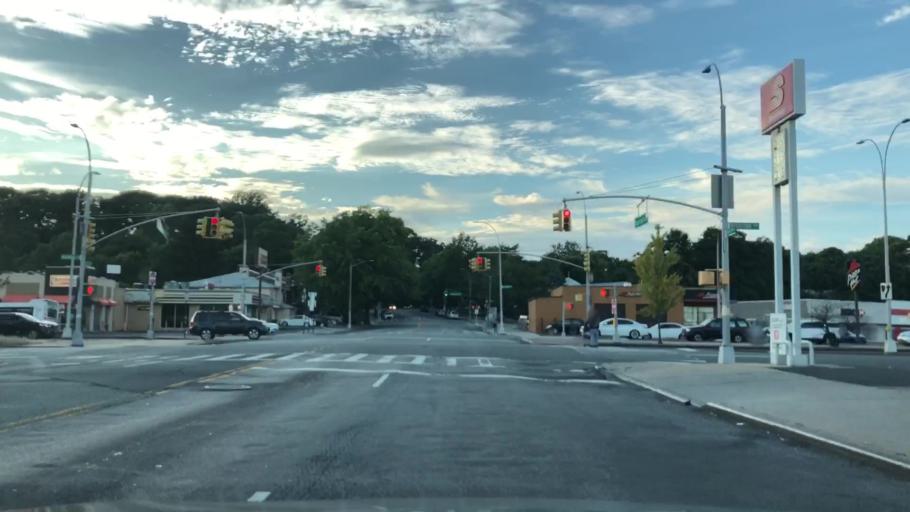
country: US
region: New York
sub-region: Nassau County
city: Bellerose Terrace
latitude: 40.7295
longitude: -73.7443
